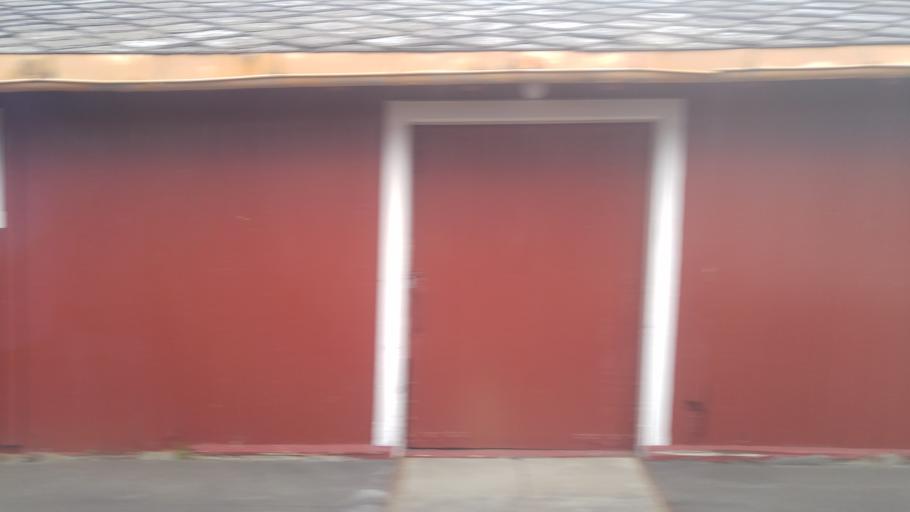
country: NO
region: Nord-Trondelag
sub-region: Stjordal
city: Stjordalshalsen
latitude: 63.4611
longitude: 11.1045
